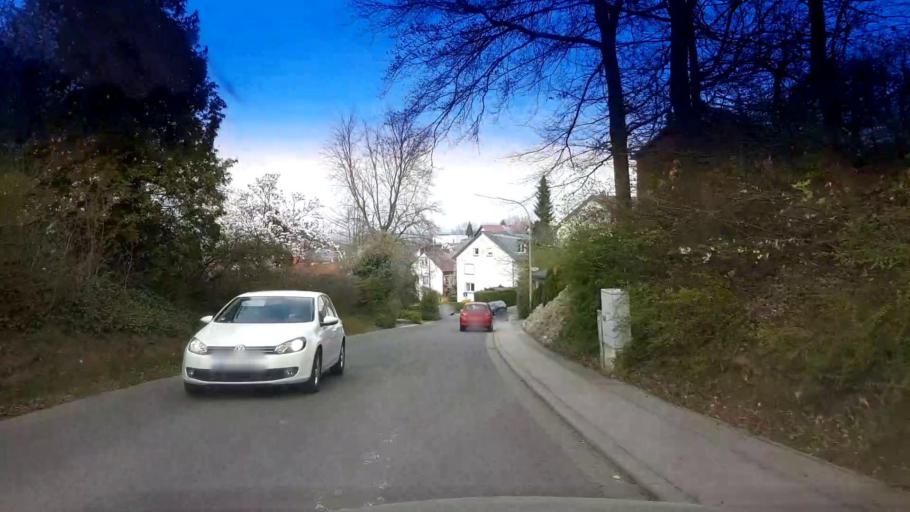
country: DE
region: Bavaria
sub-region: Upper Franconia
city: Bischberg
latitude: 49.9054
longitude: 10.8374
